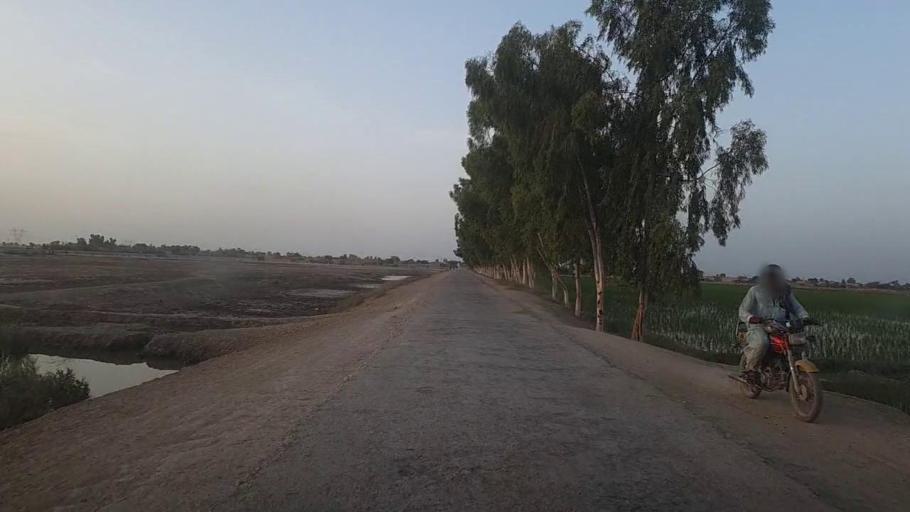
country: PK
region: Sindh
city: Radhan
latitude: 27.1276
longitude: 67.9291
